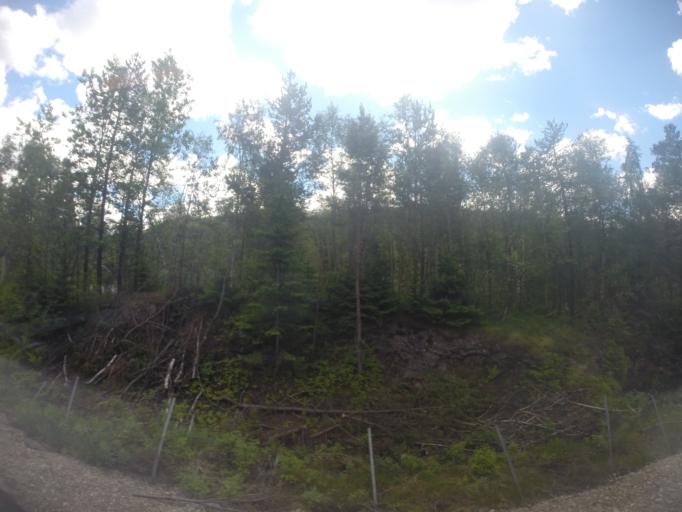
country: NO
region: Hordaland
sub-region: Granvin
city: Granvin
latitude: 60.6781
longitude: 6.7296
